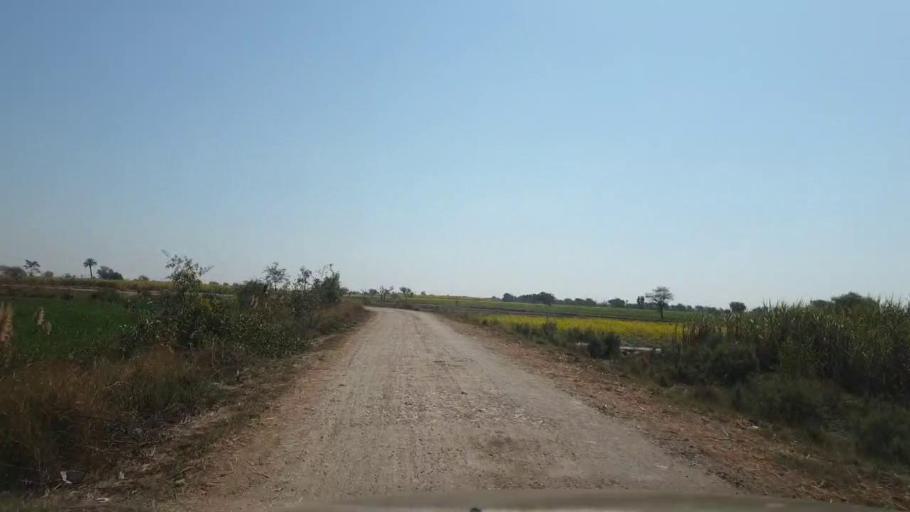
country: PK
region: Sindh
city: Mirpur Khas
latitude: 25.5654
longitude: 69.0769
